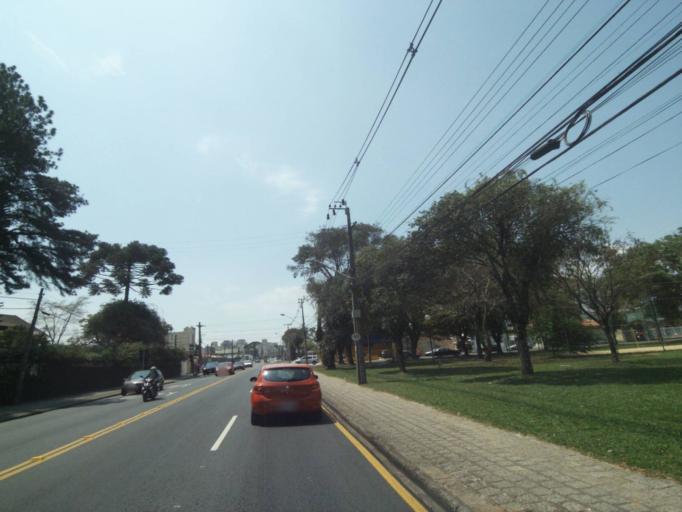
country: BR
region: Parana
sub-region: Curitiba
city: Curitiba
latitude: -25.4761
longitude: -49.3054
